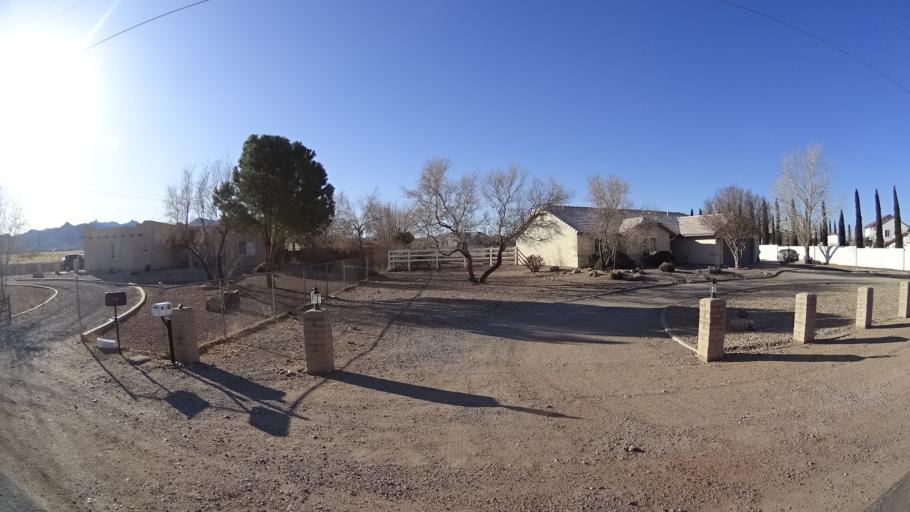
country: US
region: Arizona
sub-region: Mohave County
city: Kingman
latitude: 35.2103
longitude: -113.9944
